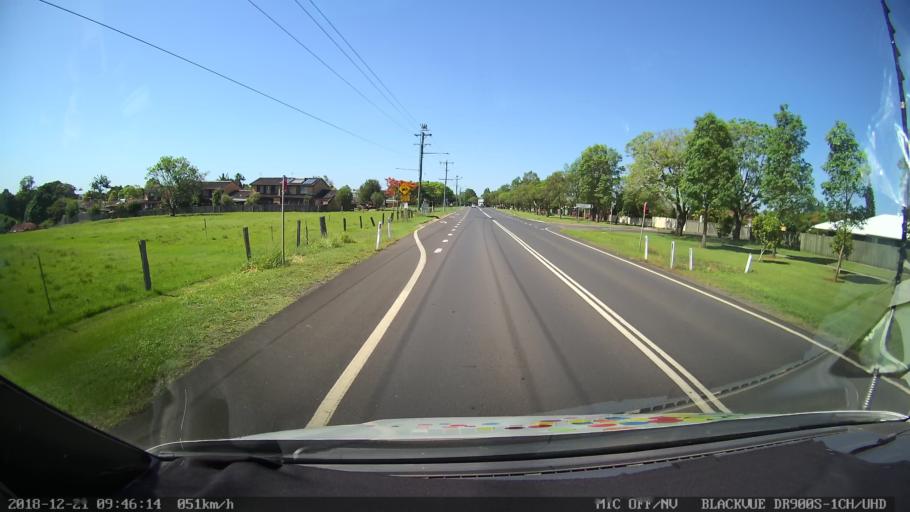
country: AU
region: New South Wales
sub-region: Clarence Valley
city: Grafton
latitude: -29.6369
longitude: 152.9266
